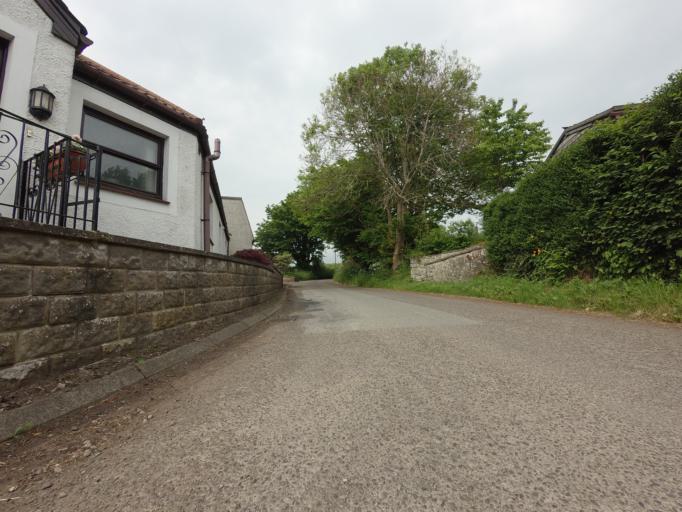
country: GB
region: Scotland
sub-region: Fife
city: Ballingry
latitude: 56.2236
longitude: -3.3462
